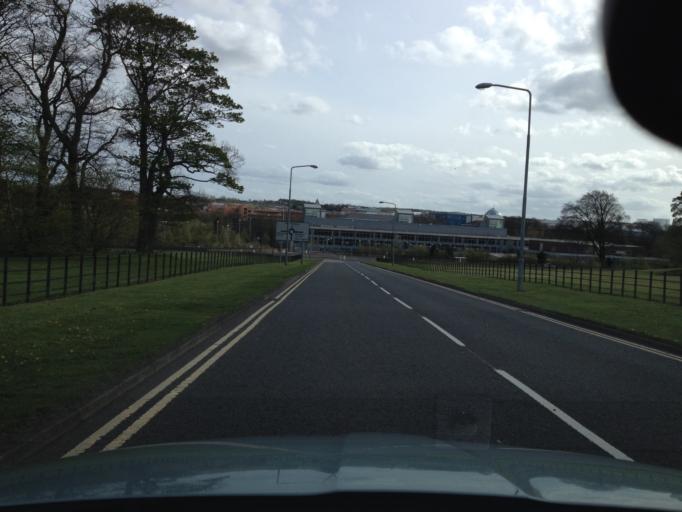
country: GB
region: Scotland
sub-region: West Lothian
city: Livingston
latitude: 55.8898
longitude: -3.5142
